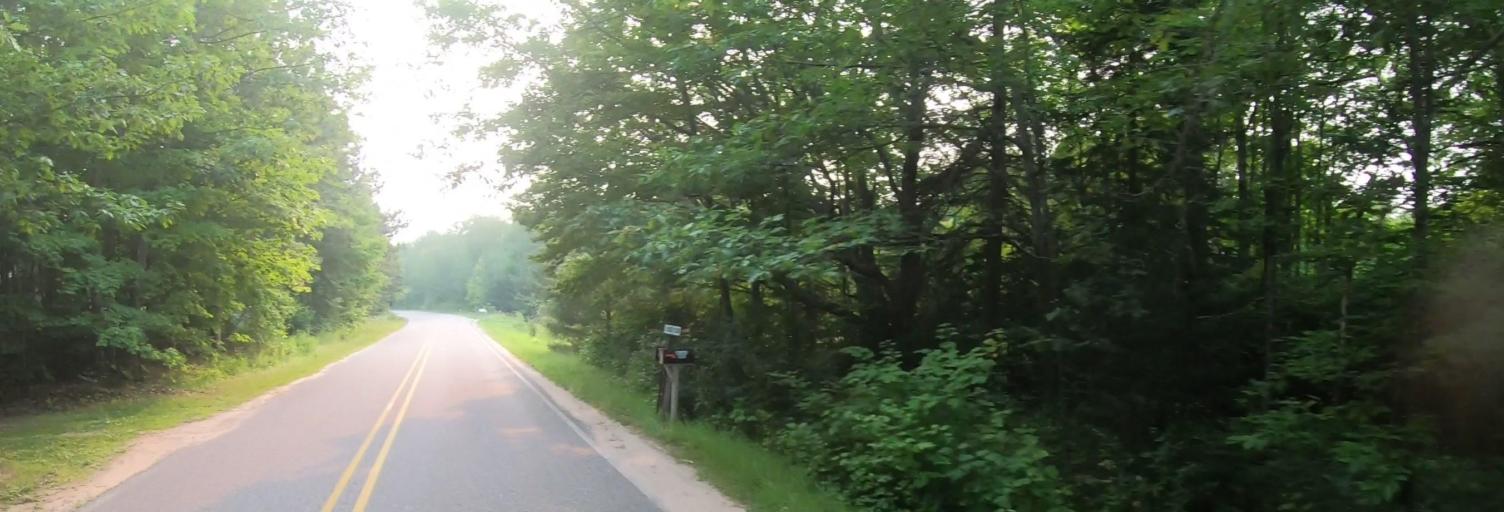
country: US
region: Michigan
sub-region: Chippewa County
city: Sault Ste. Marie
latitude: 46.4606
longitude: -84.7401
